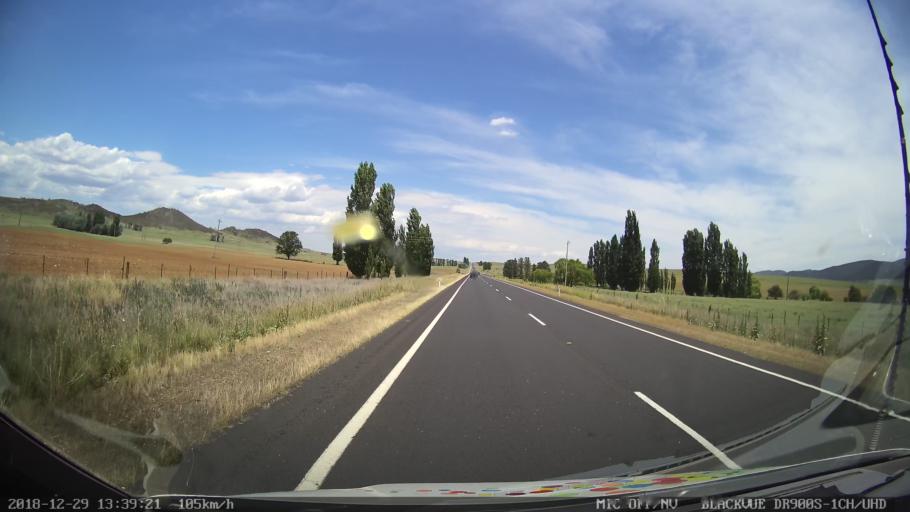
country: AU
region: New South Wales
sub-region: Cooma-Monaro
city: Cooma
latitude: -36.0117
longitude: 149.1460
